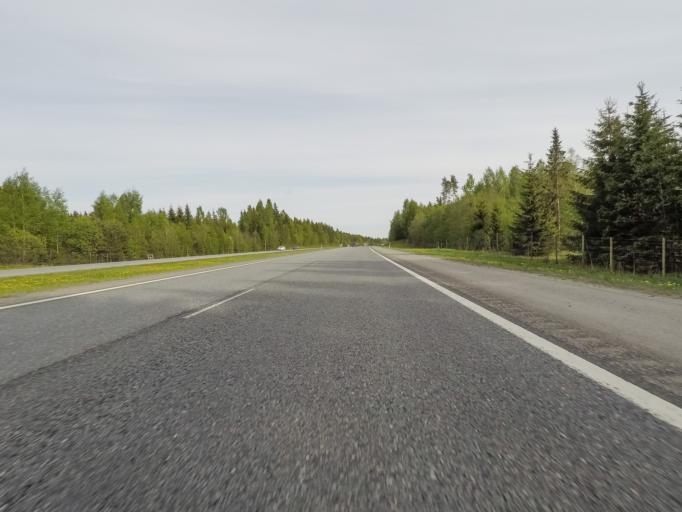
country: FI
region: Haeme
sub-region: Haemeenlinna
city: Tervakoski
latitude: 60.8363
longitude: 24.6477
